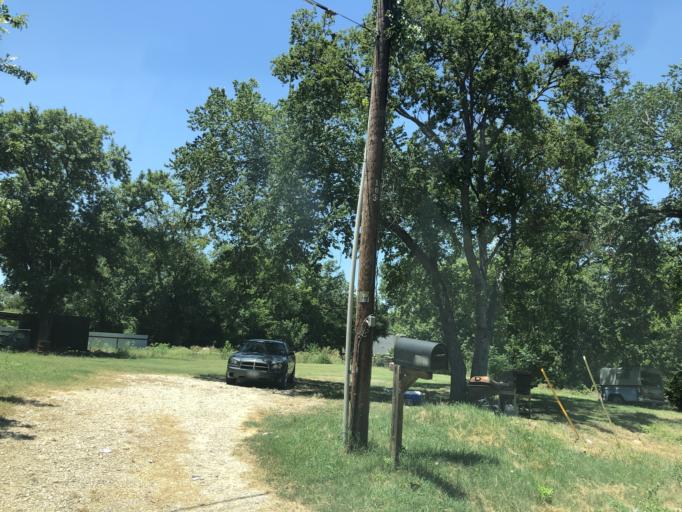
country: US
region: Texas
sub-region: Dallas County
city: Cockrell Hill
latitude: 32.7927
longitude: -96.8955
